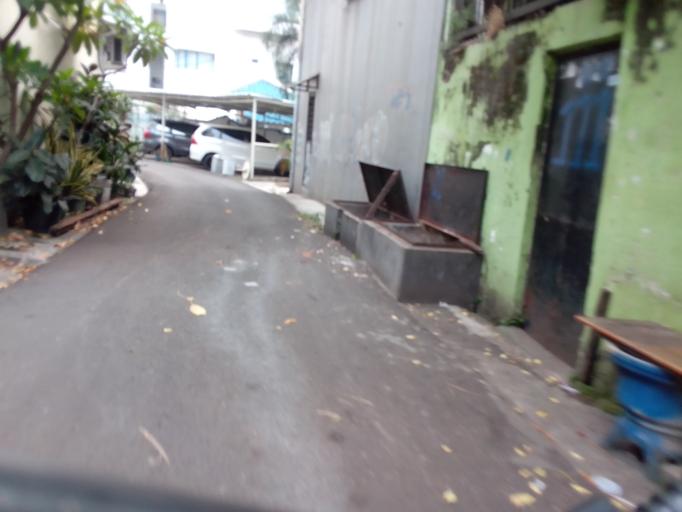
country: ID
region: Jakarta Raya
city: Jakarta
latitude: -6.2122
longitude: 106.8104
